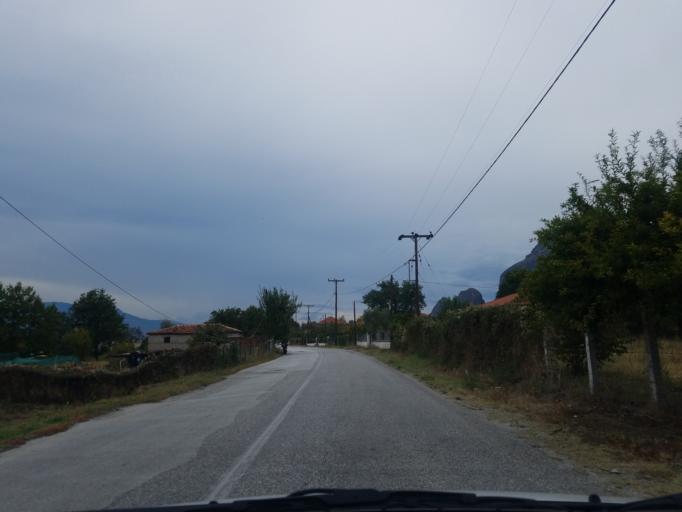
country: GR
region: Thessaly
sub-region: Trikala
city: Kalampaka
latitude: 39.6989
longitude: 21.6427
